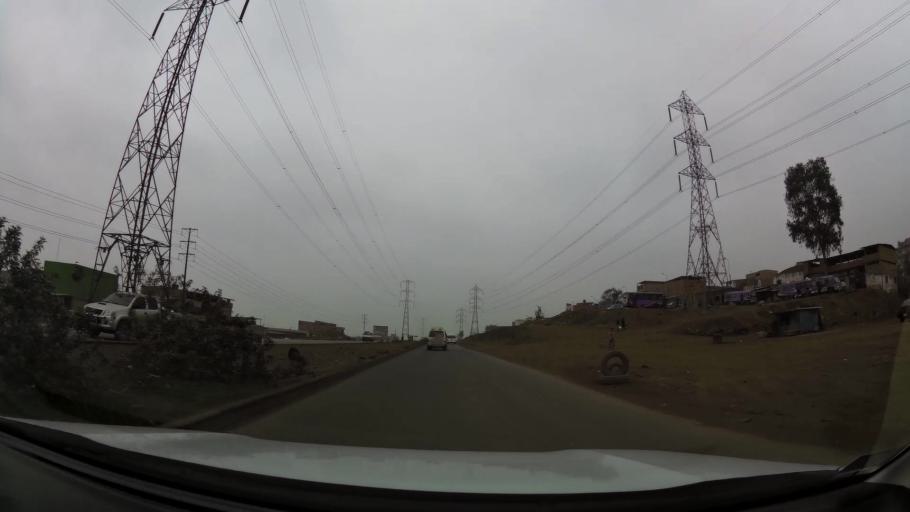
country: PE
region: Lima
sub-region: Lima
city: Surco
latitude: -12.2106
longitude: -76.9249
